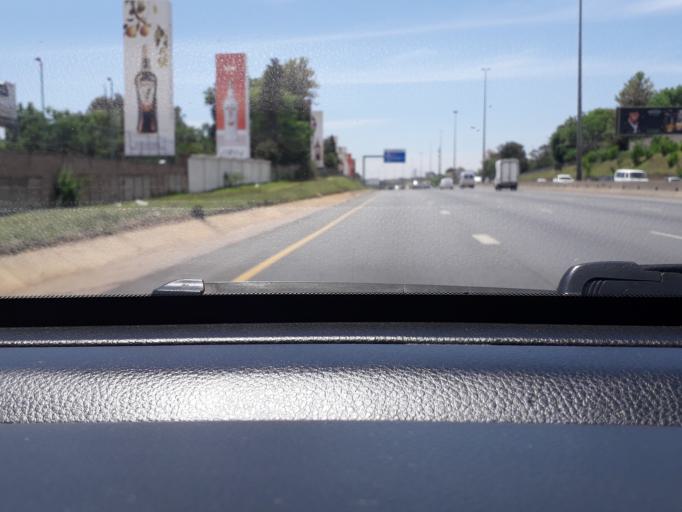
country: ZA
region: Gauteng
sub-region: City of Johannesburg Metropolitan Municipality
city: Johannesburg
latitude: -26.1180
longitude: 28.0738
